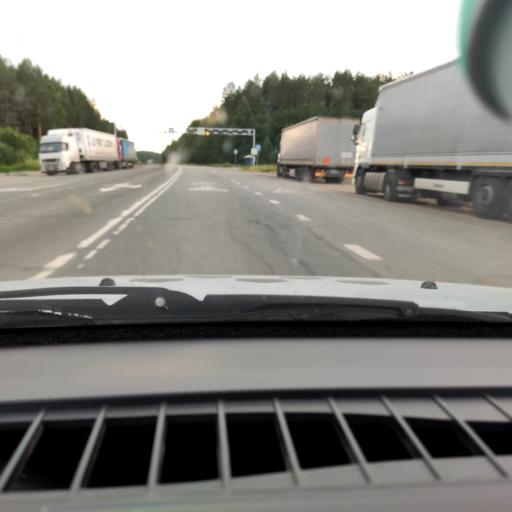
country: RU
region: Udmurtiya
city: Igra
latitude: 57.6204
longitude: 53.3684
